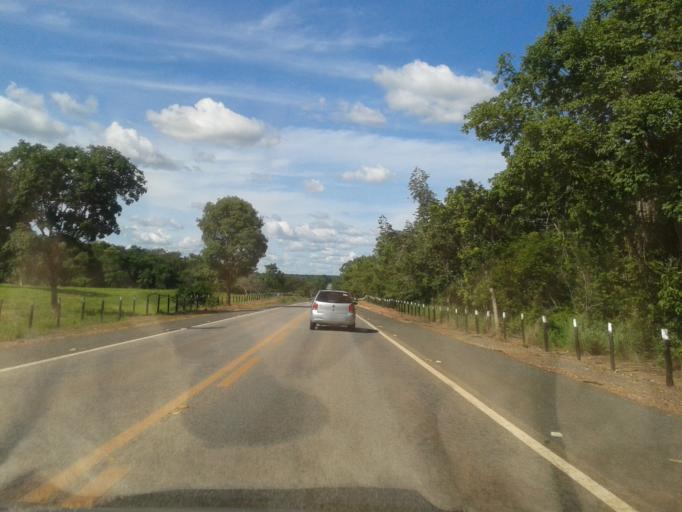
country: BR
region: Goias
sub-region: Mozarlandia
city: Mozarlandia
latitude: -15.0051
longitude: -50.5909
